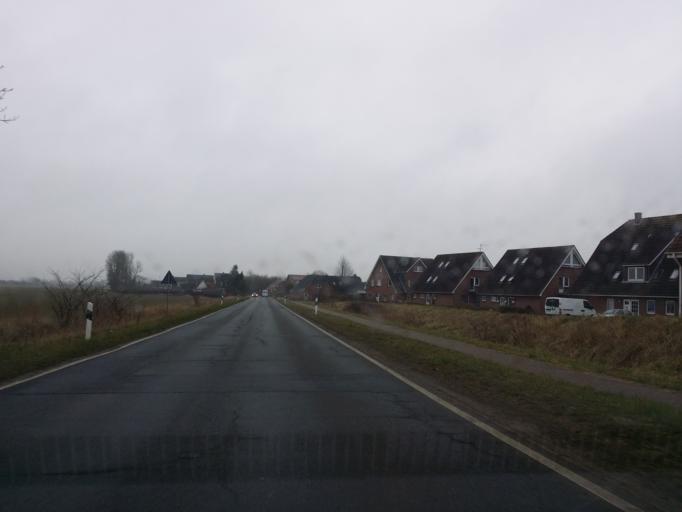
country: DE
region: Schleswig-Holstein
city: Fehmarn
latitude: 54.4501
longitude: 11.1500
